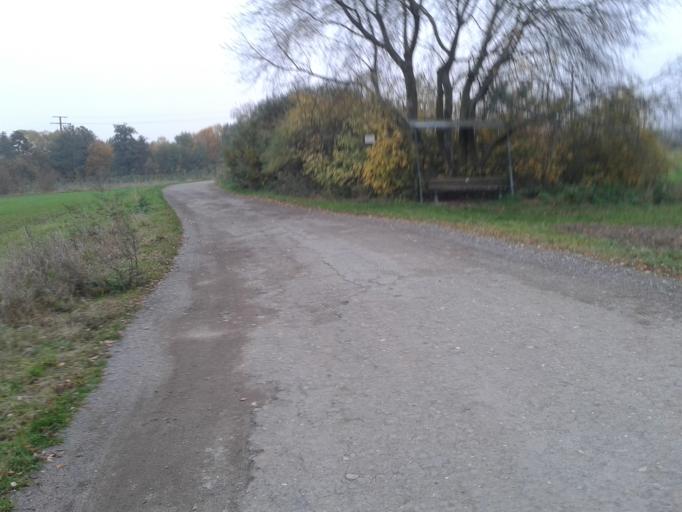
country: DE
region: Bavaria
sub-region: Upper Franconia
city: Gundelsheim
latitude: 49.9289
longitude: 10.9359
